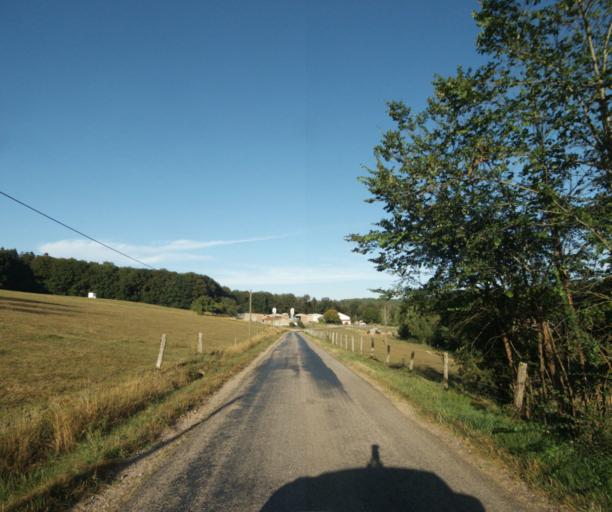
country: FR
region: Lorraine
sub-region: Departement des Vosges
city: Urimenil
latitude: 48.1367
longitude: 6.4038
